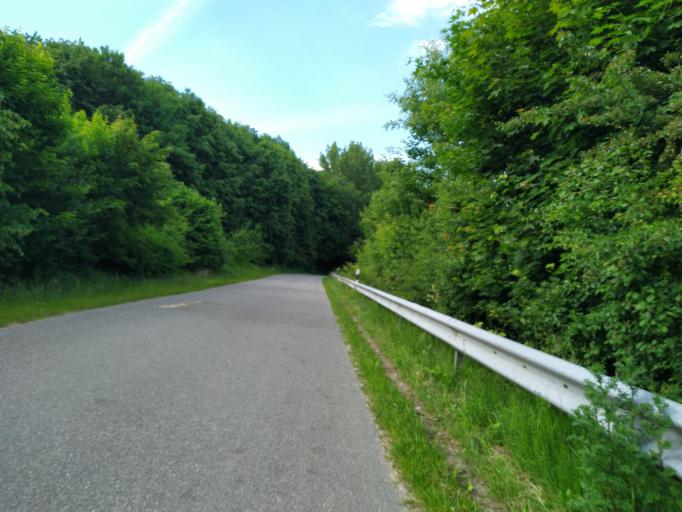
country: DE
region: Schleswig-Holstein
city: Gross Gronau
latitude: 53.7927
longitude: 10.7263
